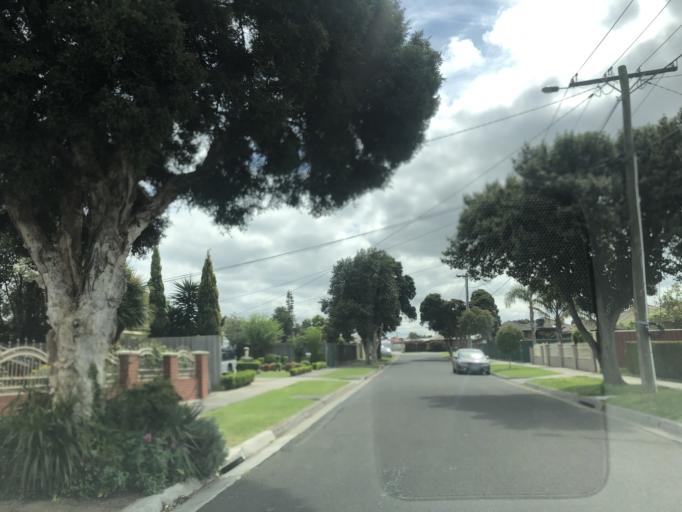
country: AU
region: Victoria
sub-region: Greater Dandenong
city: Dandenong North
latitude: -37.9549
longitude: 145.2104
